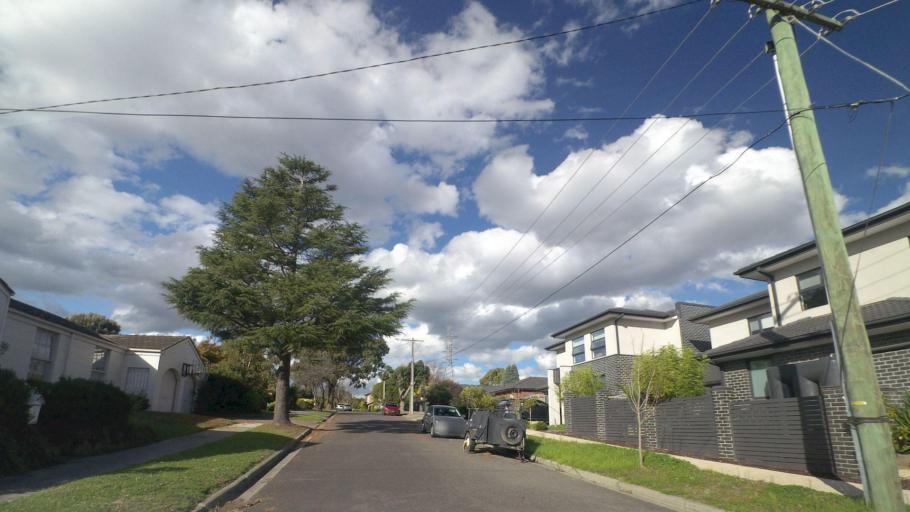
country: AU
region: Victoria
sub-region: Manningham
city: Doncaster East
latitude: -37.7814
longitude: 145.1409
